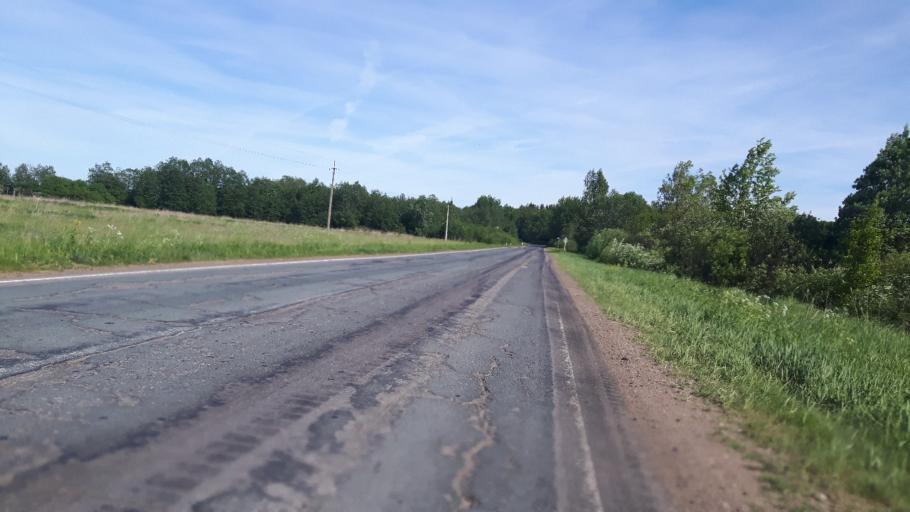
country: RU
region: Leningrad
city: Ivangorod
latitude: 59.4180
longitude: 28.3628
